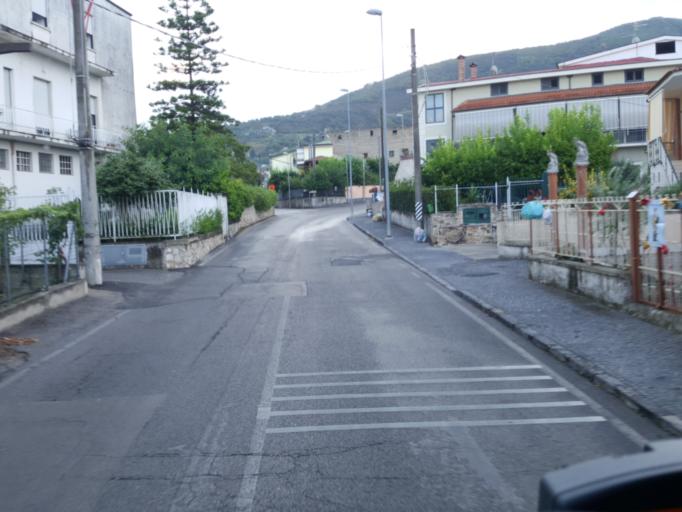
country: IT
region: Campania
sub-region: Provincia di Napoli
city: Carbonara di Nola
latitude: 40.8809
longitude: 14.5743
